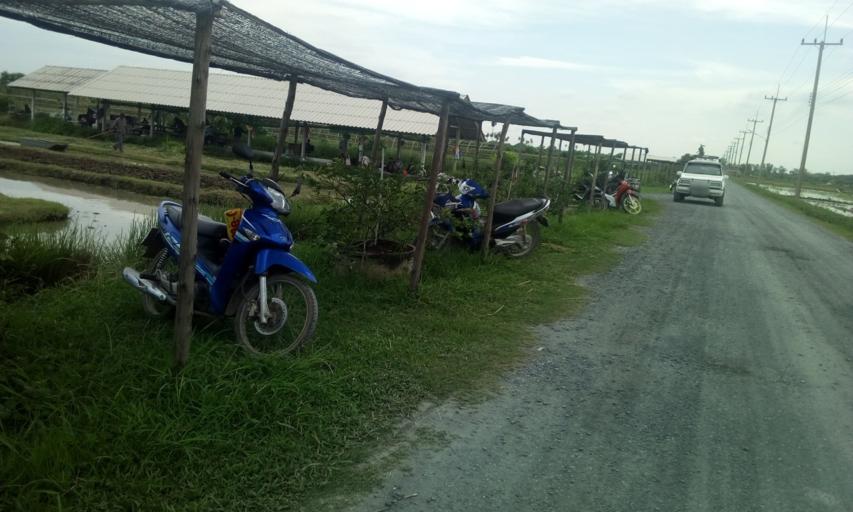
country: TH
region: Pathum Thani
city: Ban Lam Luk Ka
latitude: 13.9896
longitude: 100.8412
